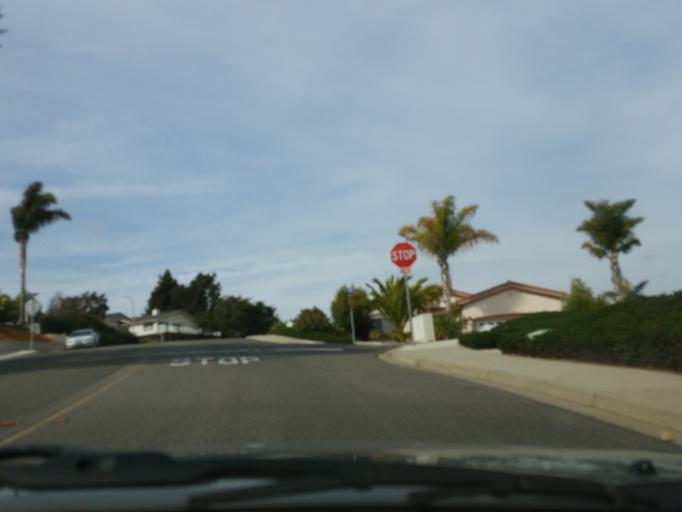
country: US
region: California
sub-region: San Luis Obispo County
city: Pismo Beach
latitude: 35.1397
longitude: -120.6287
